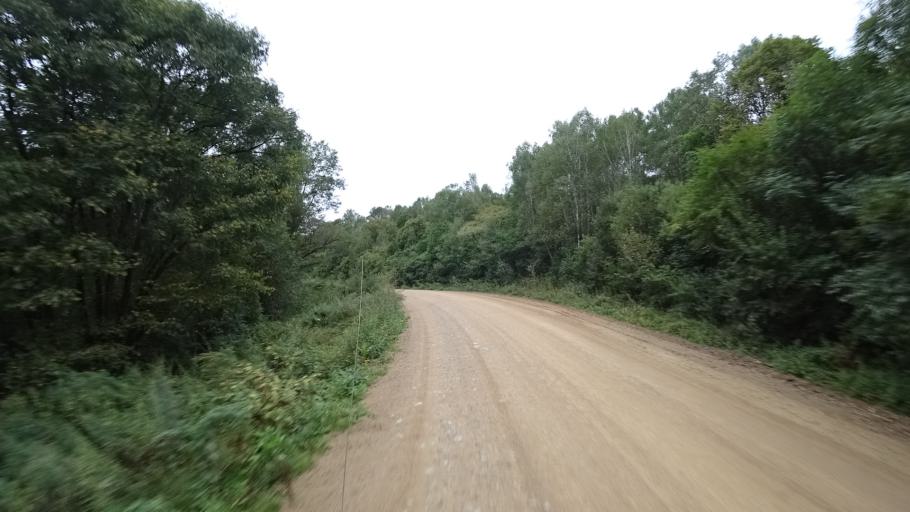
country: RU
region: Primorskiy
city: Rettikhovka
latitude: 44.1797
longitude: 132.8572
